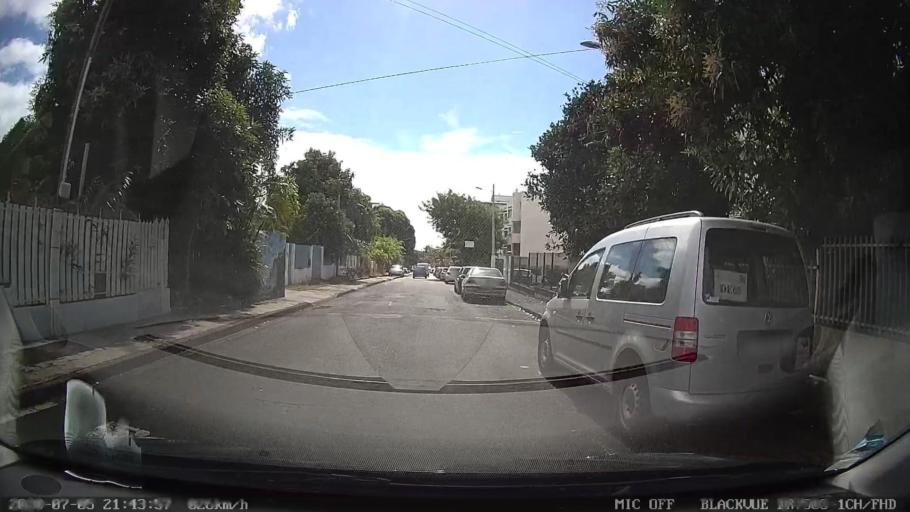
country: RE
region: Reunion
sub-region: Reunion
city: Saint-Denis
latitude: -20.8888
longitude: 55.4798
